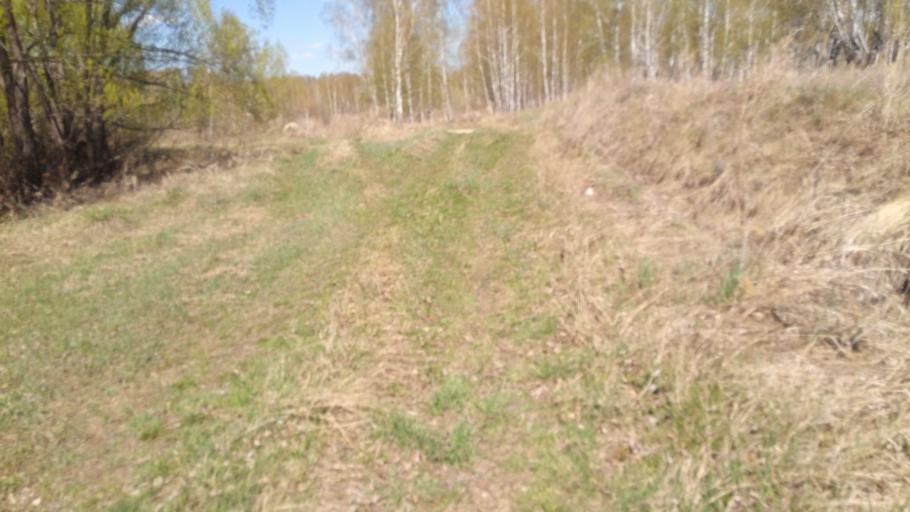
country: RU
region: Chelyabinsk
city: Timiryazevskiy
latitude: 55.0008
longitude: 60.8519
